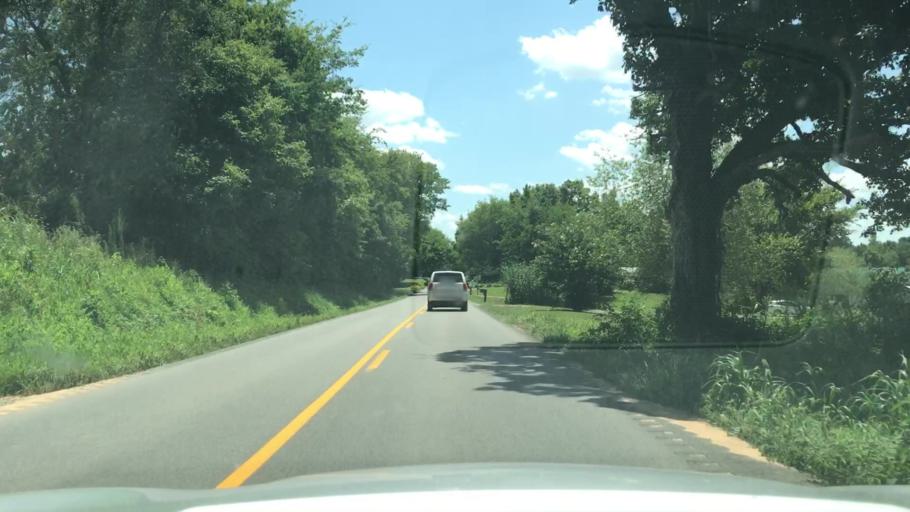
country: US
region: Kentucky
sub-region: Christian County
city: Hopkinsville
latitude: 36.8998
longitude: -87.4494
